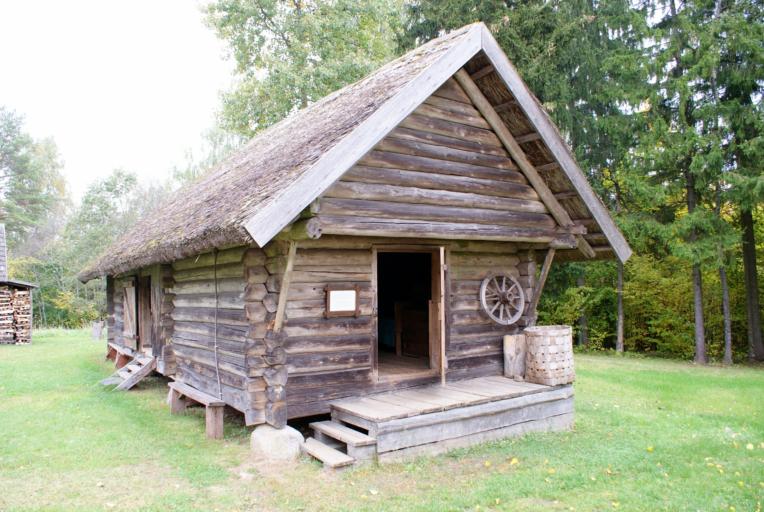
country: LV
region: Dagda
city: Dagda
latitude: 56.1903
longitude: 27.3974
